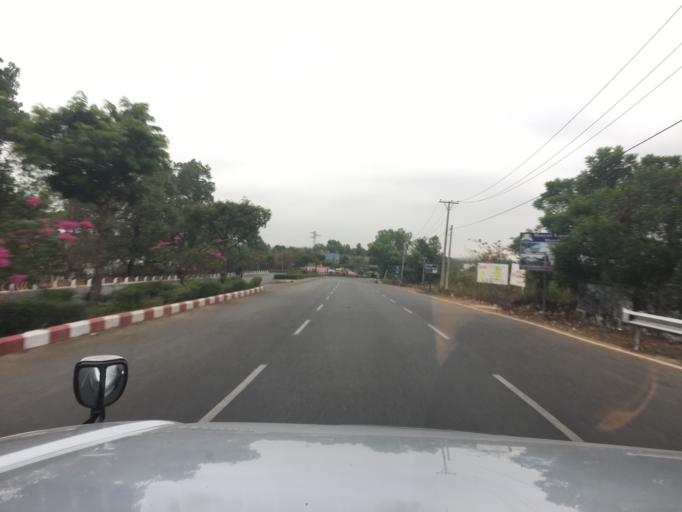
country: MM
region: Bago
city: Thanatpin
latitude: 17.2145
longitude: 96.4226
